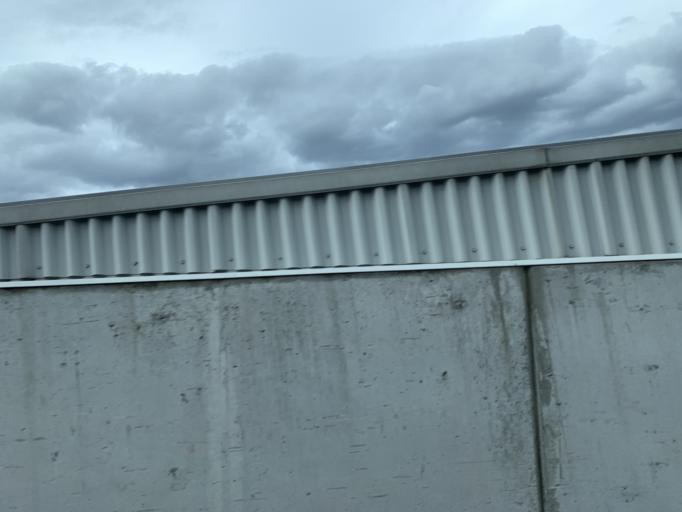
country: AU
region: Victoria
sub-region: Manningham
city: Doncaster
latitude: -37.7849
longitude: 145.1274
